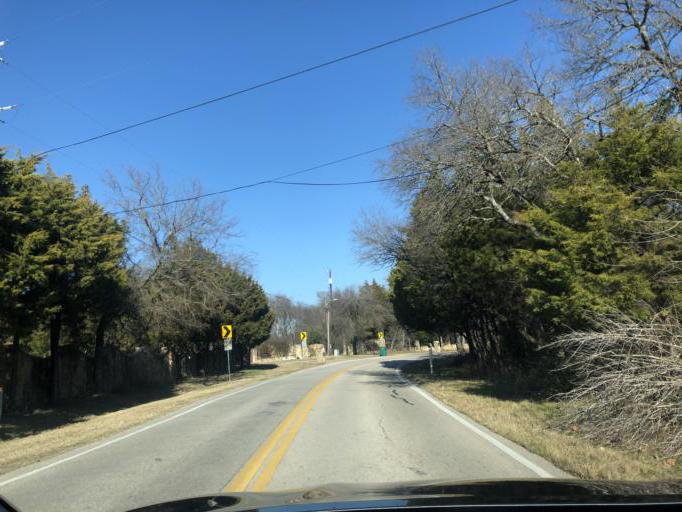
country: US
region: Texas
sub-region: Dallas County
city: Cedar Hill
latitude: 32.6191
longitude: -96.9328
